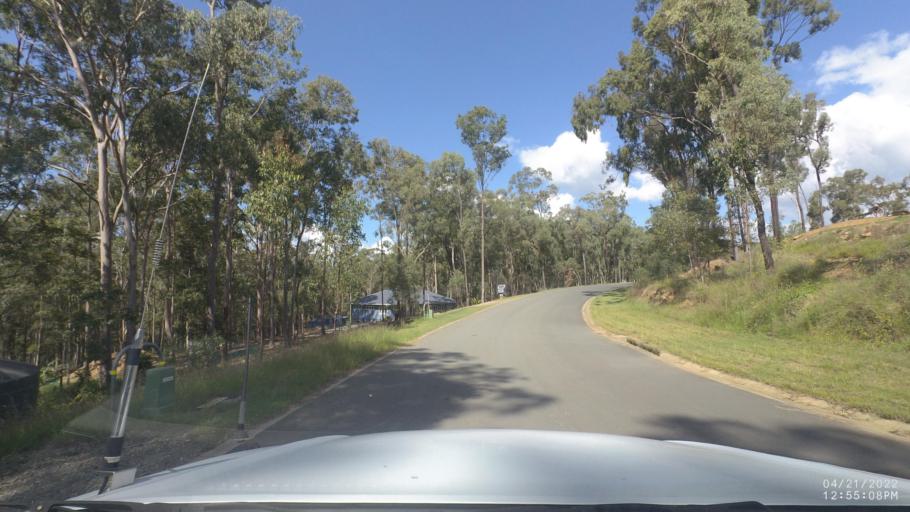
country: AU
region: Queensland
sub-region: Logan
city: Cedar Vale
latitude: -27.8353
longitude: 153.1006
